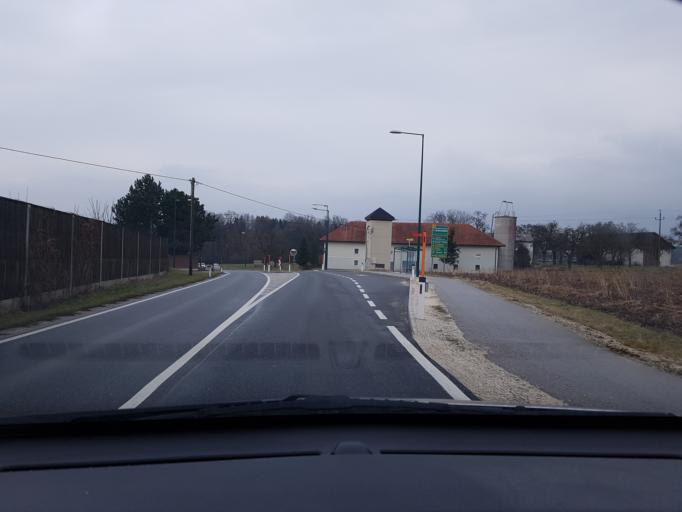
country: AT
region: Upper Austria
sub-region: Steyr Stadt
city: Steyr
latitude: 48.0815
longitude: 14.3707
